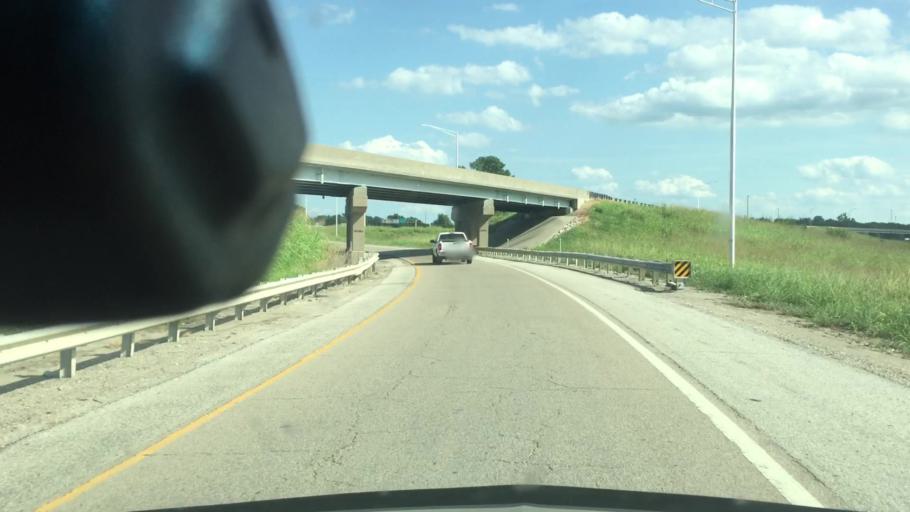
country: US
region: Illinois
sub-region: Saint Clair County
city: East Saint Louis
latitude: 38.6482
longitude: -90.1322
